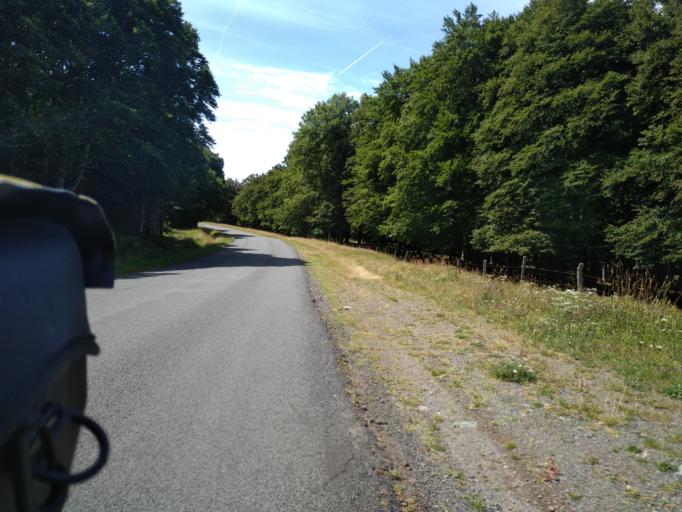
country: FR
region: Midi-Pyrenees
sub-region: Departement de l'Aveyron
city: Laguiole
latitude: 44.6637
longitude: 2.9587
